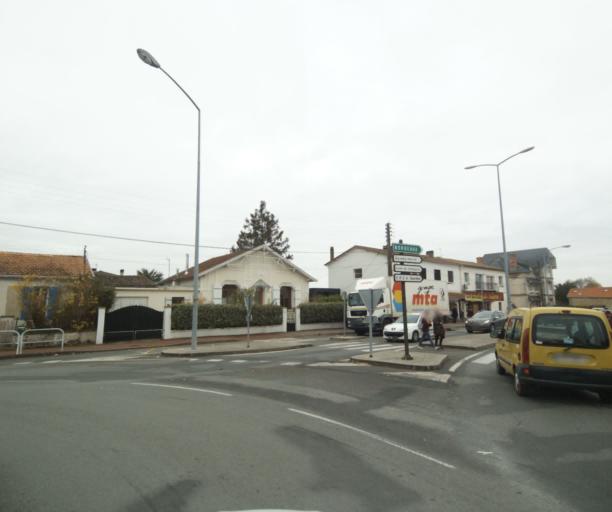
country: FR
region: Poitou-Charentes
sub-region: Departement de la Charente-Maritime
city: Saintes
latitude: 45.7368
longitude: -0.6443
